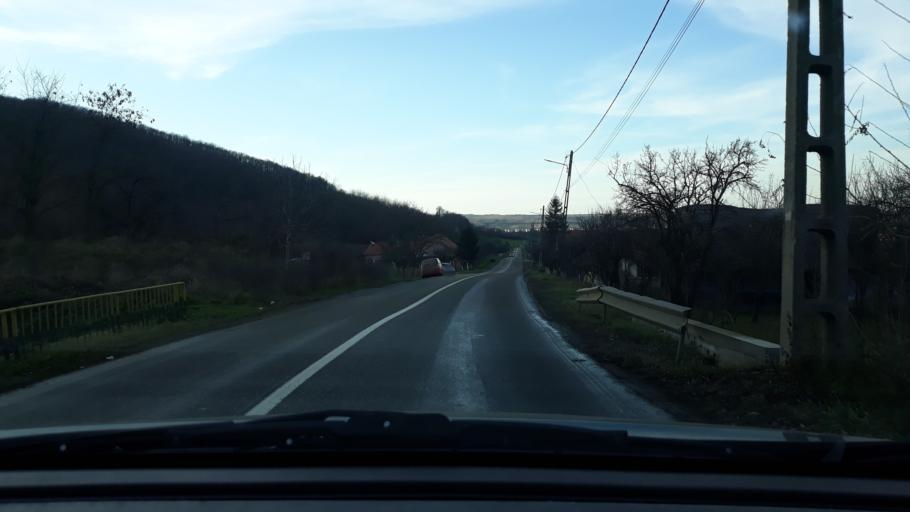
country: RO
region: Salaj
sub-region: Comuna Marca
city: Marca
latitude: 47.2294
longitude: 22.5502
